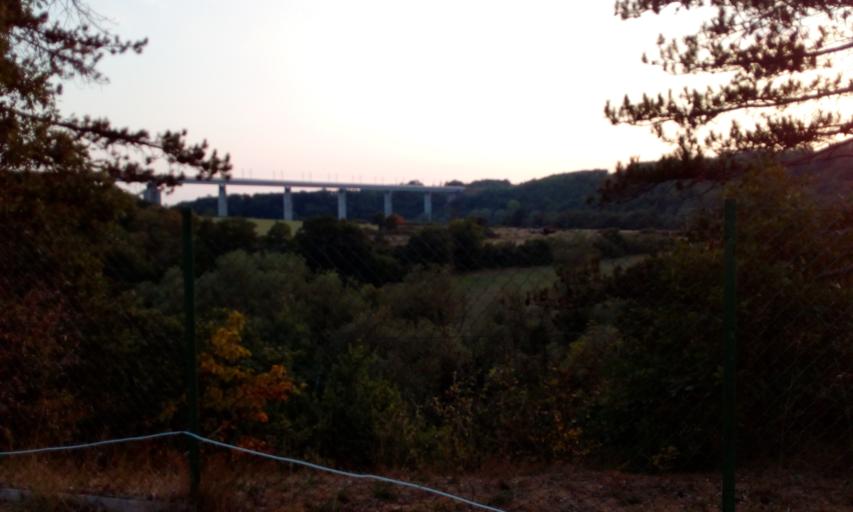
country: FR
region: Lorraine
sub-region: Departement de Meurthe-et-Moselle
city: Pagny-sur-Moselle
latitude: 48.9655
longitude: 5.8844
